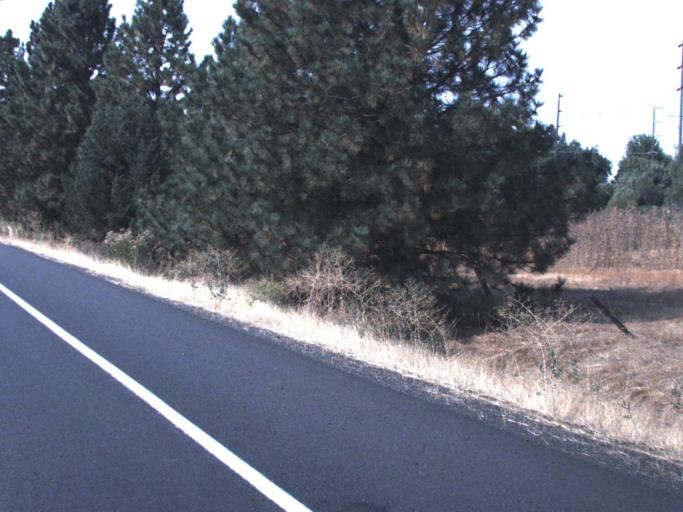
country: US
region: Washington
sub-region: Whitman County
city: Pullman
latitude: 46.7107
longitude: -117.2006
